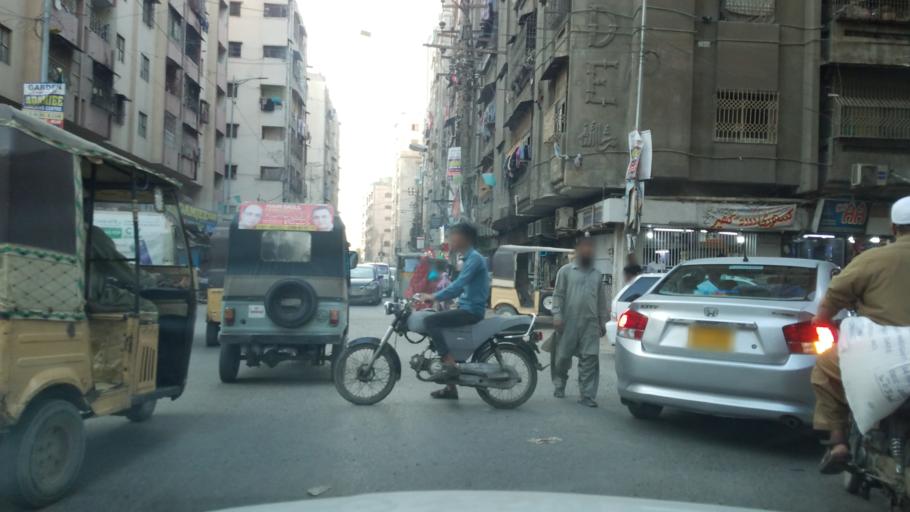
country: PK
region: Sindh
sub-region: Karachi District
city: Karachi
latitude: 24.8777
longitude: 67.0197
